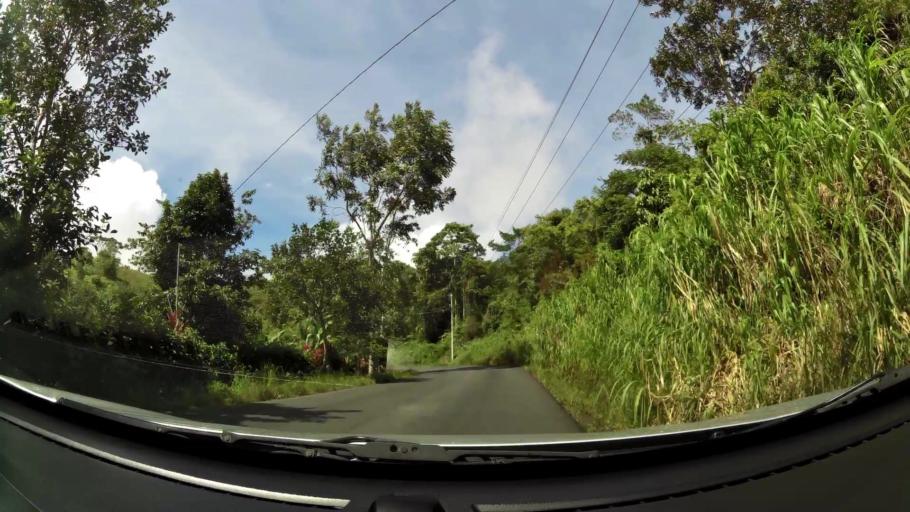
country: CR
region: San Jose
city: San Isidro
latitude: 9.3282
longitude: -83.7503
